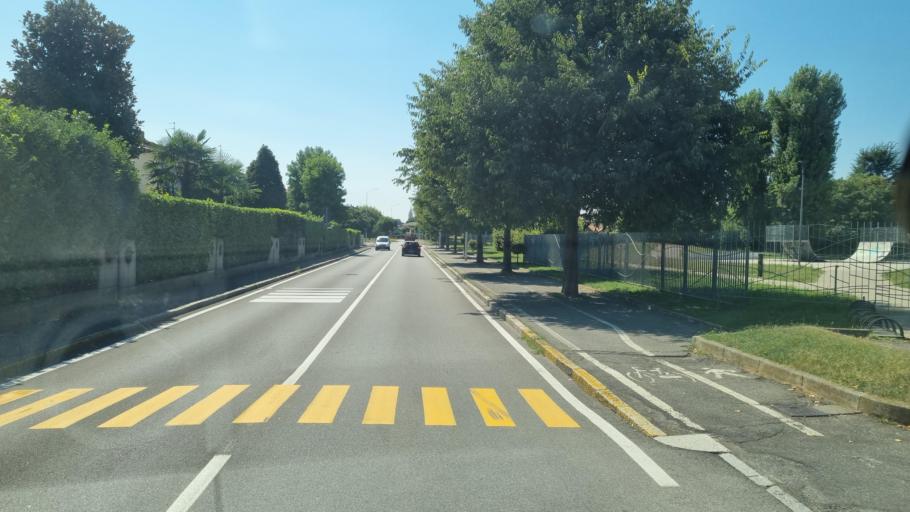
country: IT
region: Lombardy
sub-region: Provincia di Bergamo
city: Azzano San Paolo
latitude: 45.6580
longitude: 9.6706
